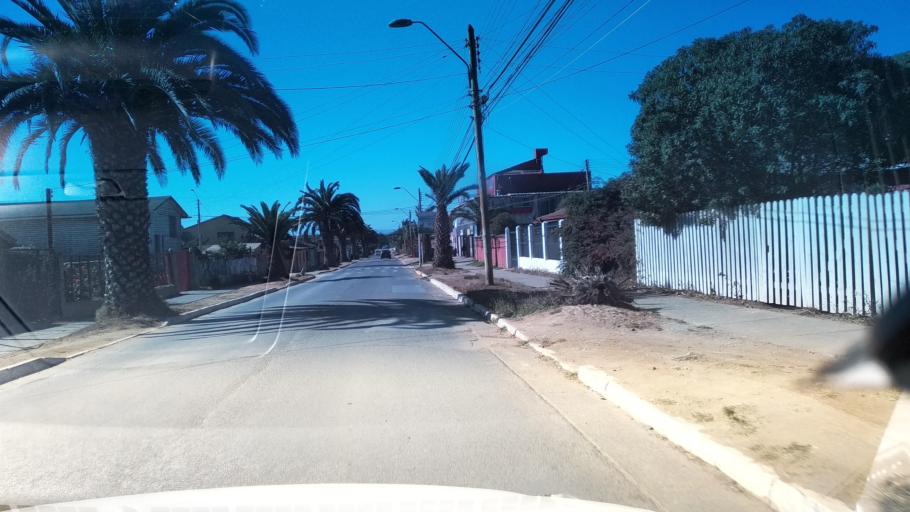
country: CL
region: O'Higgins
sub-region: Provincia de Colchagua
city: Santa Cruz
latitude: -34.3913
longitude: -72.0146
